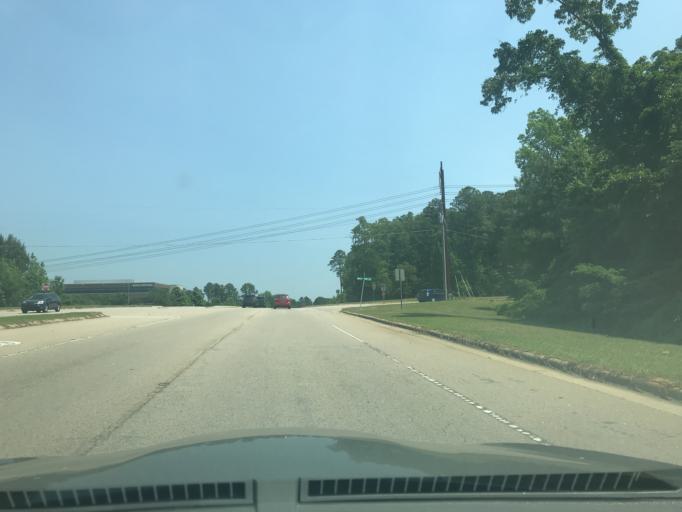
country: US
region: North Carolina
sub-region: Wake County
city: West Raleigh
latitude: 35.8194
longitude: -78.7115
